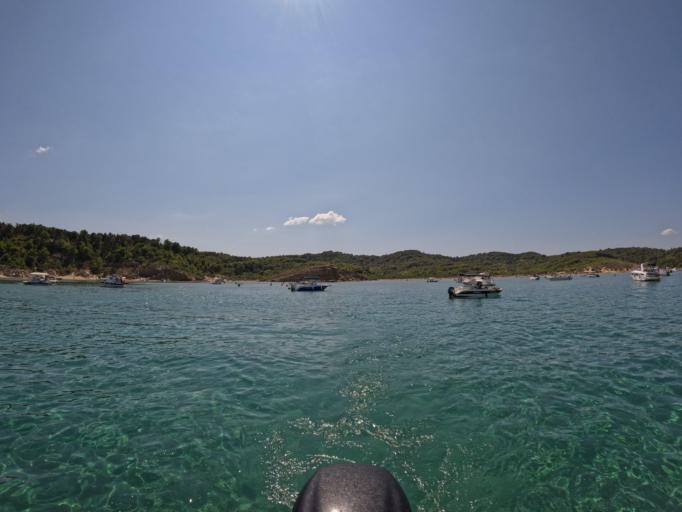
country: HR
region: Primorsko-Goranska
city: Lopar
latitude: 44.8420
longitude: 14.7548
